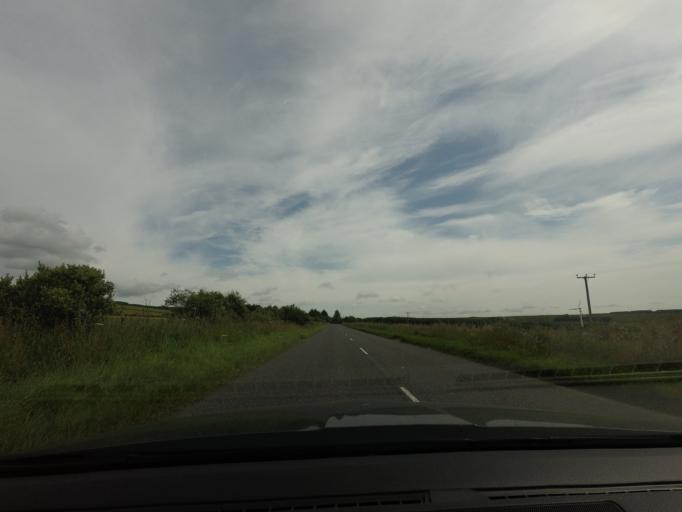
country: GB
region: Scotland
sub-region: Aberdeenshire
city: Turriff
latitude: 57.5969
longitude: -2.2925
